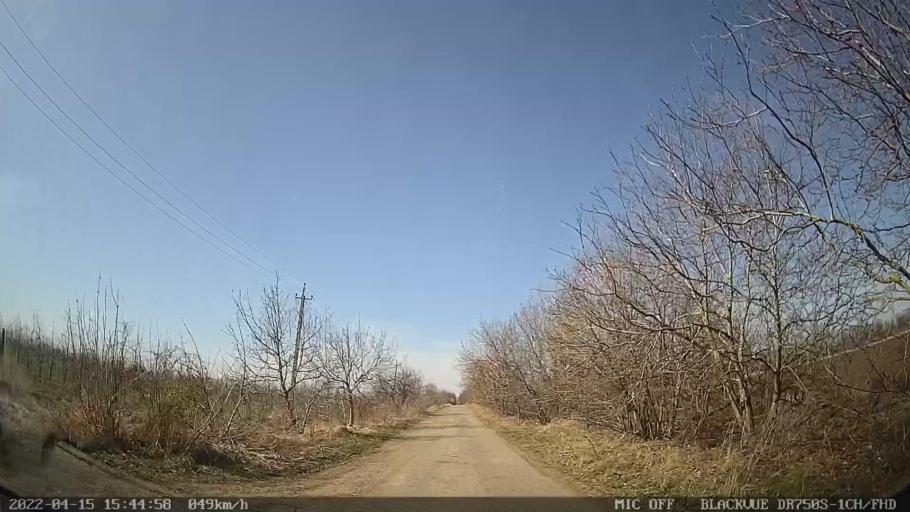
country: MD
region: Raionul Ocnita
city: Otaci
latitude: 48.3733
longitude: 27.9204
